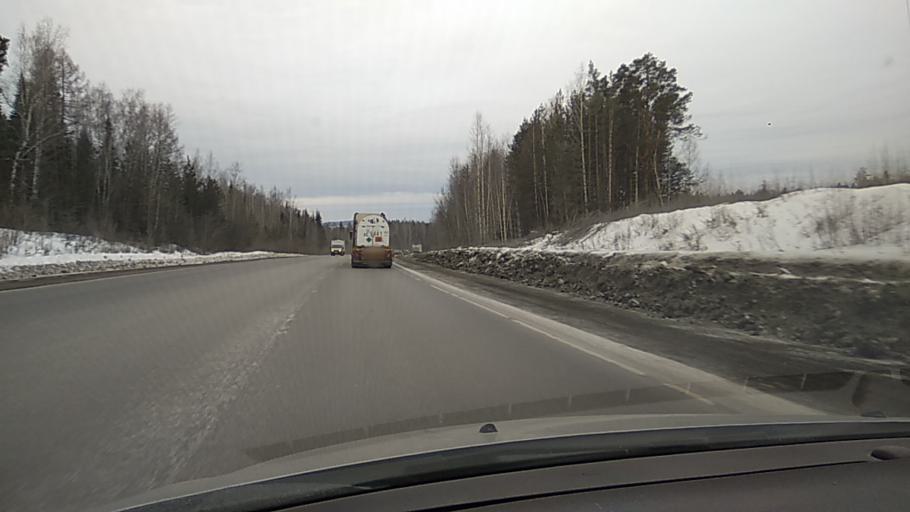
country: RU
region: Sverdlovsk
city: Talitsa
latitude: 56.8294
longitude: 59.9935
